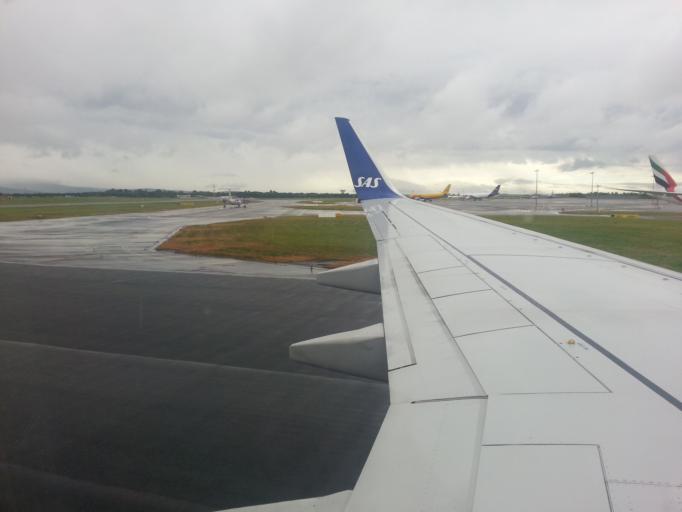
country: IE
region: Leinster
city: Ballymun
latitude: 53.4270
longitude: -6.2548
